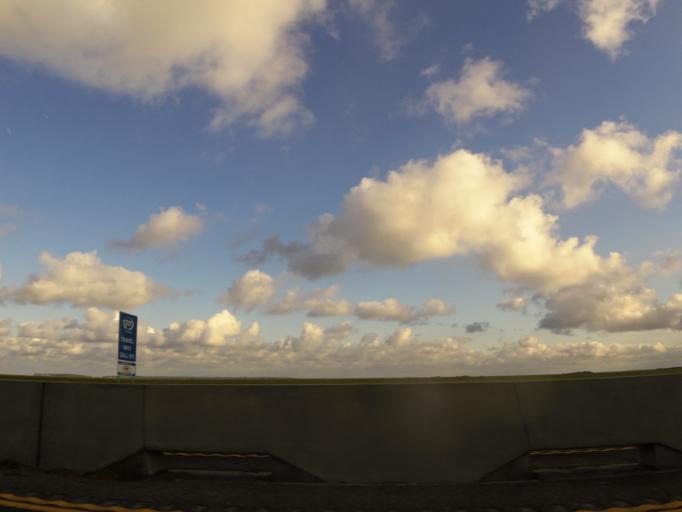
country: US
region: Georgia
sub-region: Glynn County
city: Brunswick
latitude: 31.1627
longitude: -81.4563
